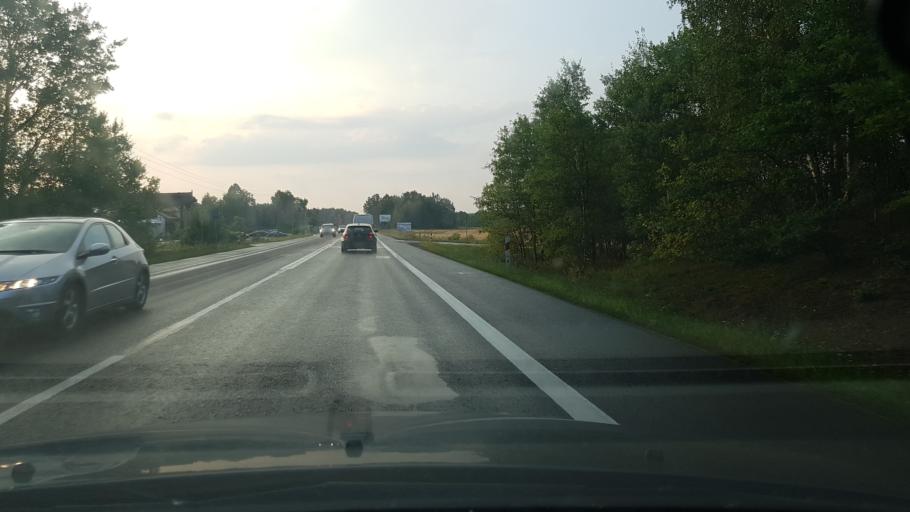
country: PL
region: Masovian Voivodeship
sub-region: Powiat ciechanowski
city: Glinojeck
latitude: 52.8157
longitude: 20.2657
